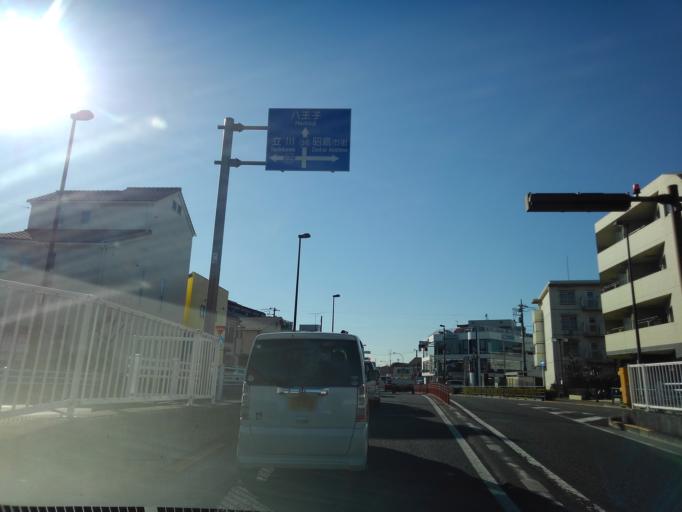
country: JP
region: Tokyo
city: Hino
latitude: 35.7075
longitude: 139.3781
